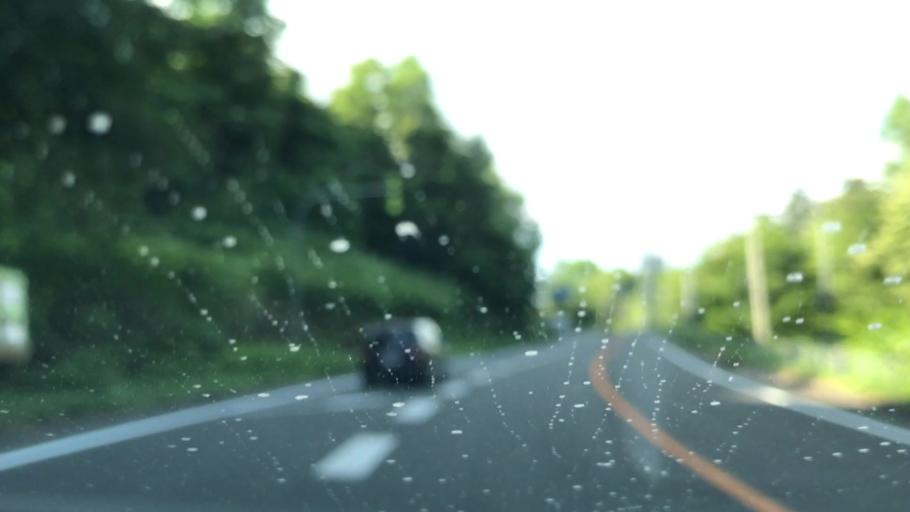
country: JP
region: Hokkaido
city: Shimo-furano
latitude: 42.9050
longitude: 142.4191
